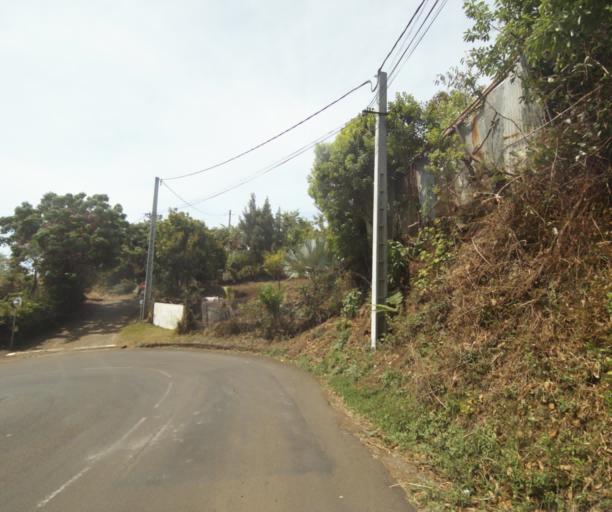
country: RE
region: Reunion
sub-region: Reunion
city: Trois-Bassins
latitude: -21.0698
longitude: 55.2908
